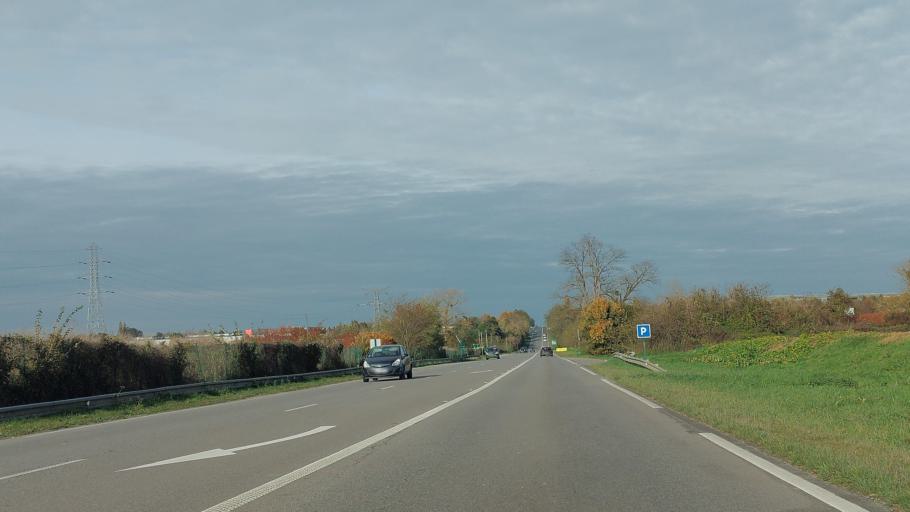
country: FR
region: Ile-de-France
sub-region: Departement du Val-d'Oise
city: Survilliers
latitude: 49.0821
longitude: 2.5297
